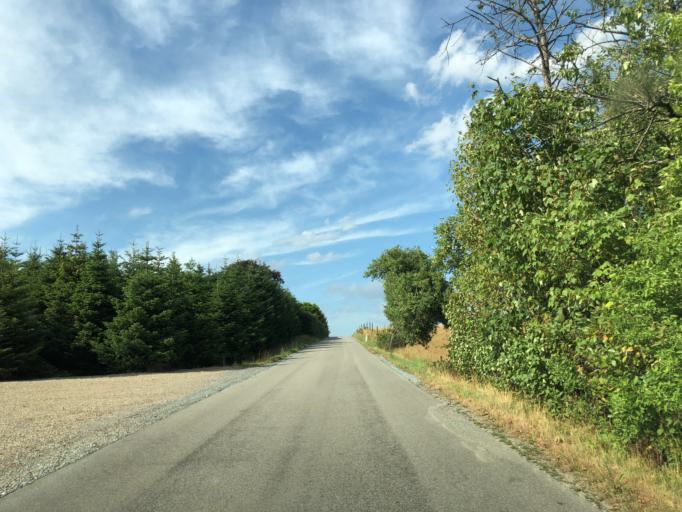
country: DK
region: South Denmark
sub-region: Vejle Kommune
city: Egtved
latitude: 55.6725
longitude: 9.3032
